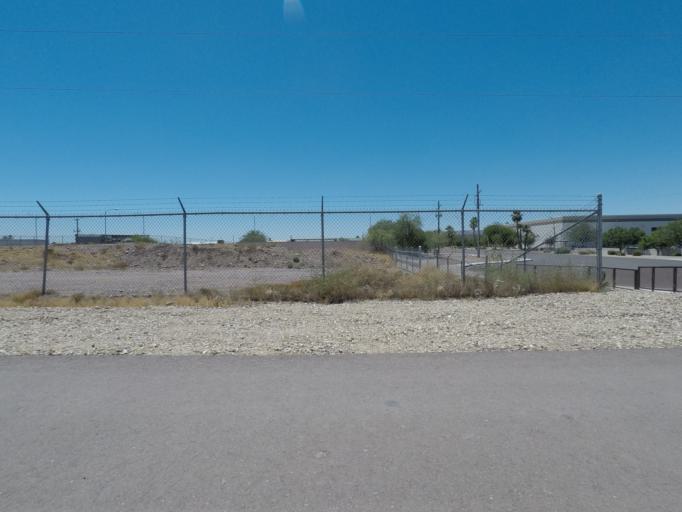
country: US
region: Arizona
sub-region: Maricopa County
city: Tempe Junction
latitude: 33.4261
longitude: -111.9952
